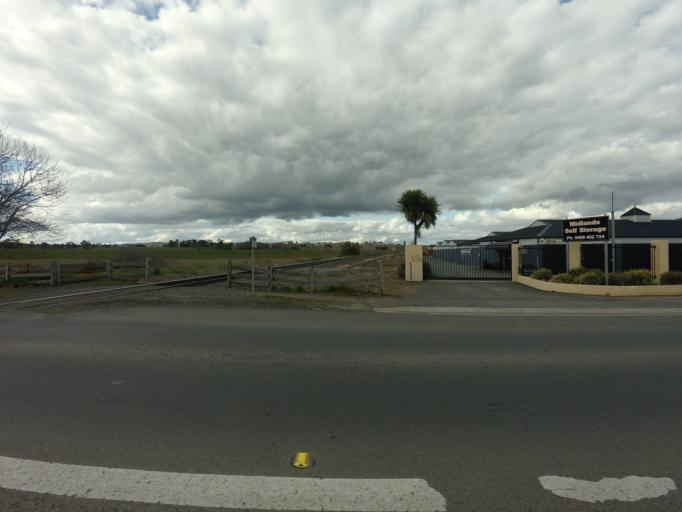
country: AU
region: Tasmania
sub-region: Northern Midlands
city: Longford
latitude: -41.5874
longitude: 147.1187
